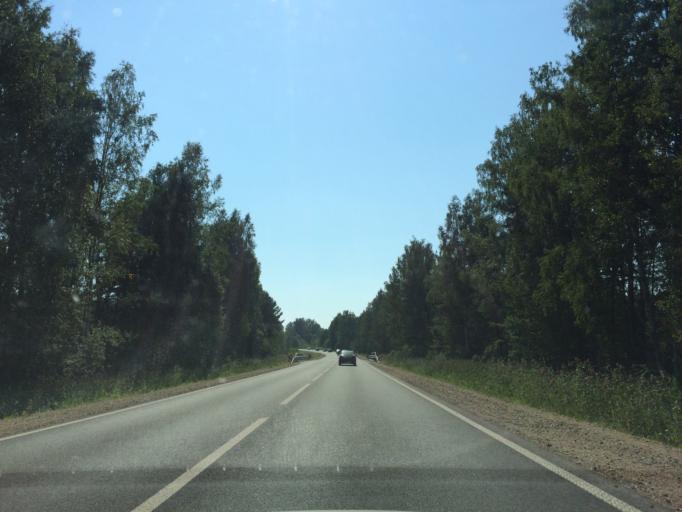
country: LV
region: Rezekne
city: Rezekne
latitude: 56.3658
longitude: 27.1825
